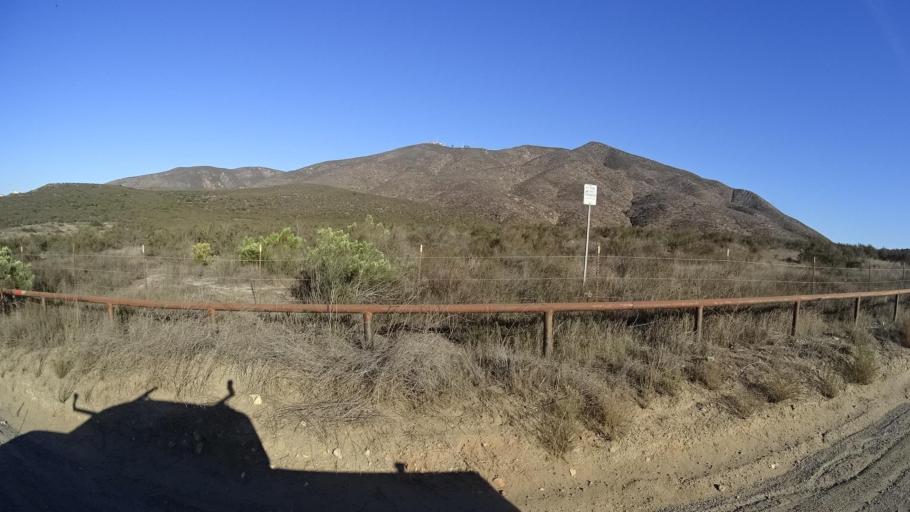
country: US
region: California
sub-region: San Diego County
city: Jamul
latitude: 32.6780
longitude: -116.9180
